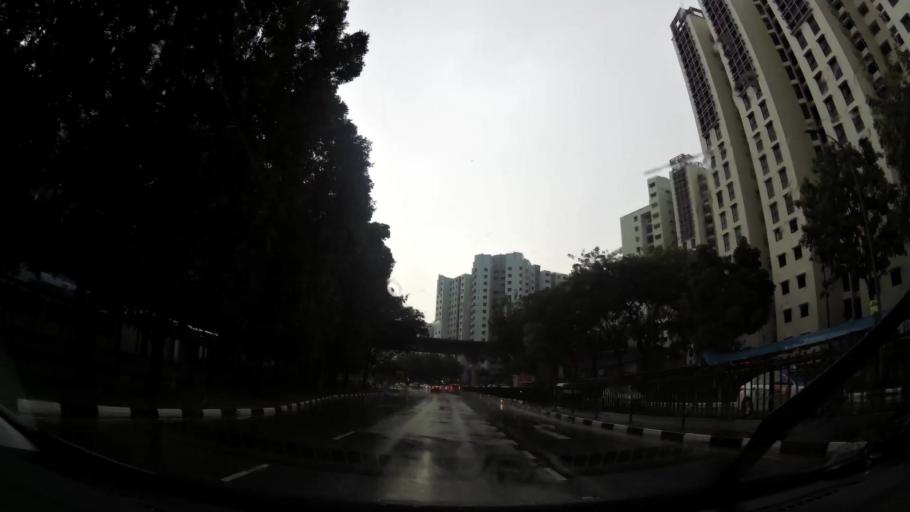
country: MY
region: Johor
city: Kampung Pasir Gudang Baru
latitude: 1.3950
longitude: 103.9022
